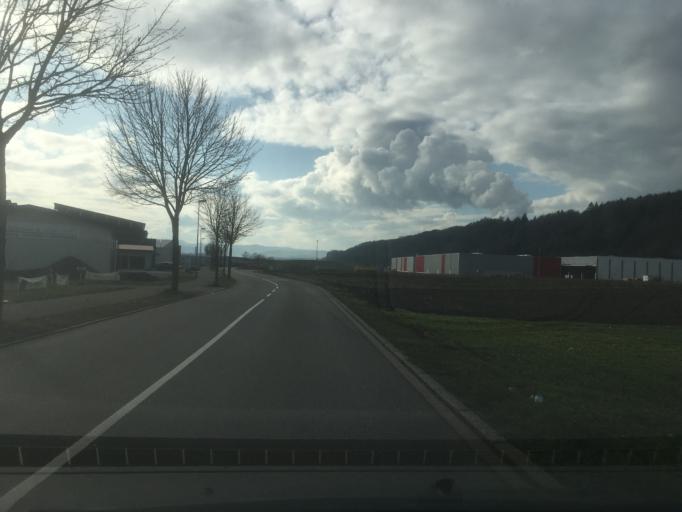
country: CH
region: Aargau
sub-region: Bezirk Zurzach
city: Koblenz
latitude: 47.6260
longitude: 8.2530
